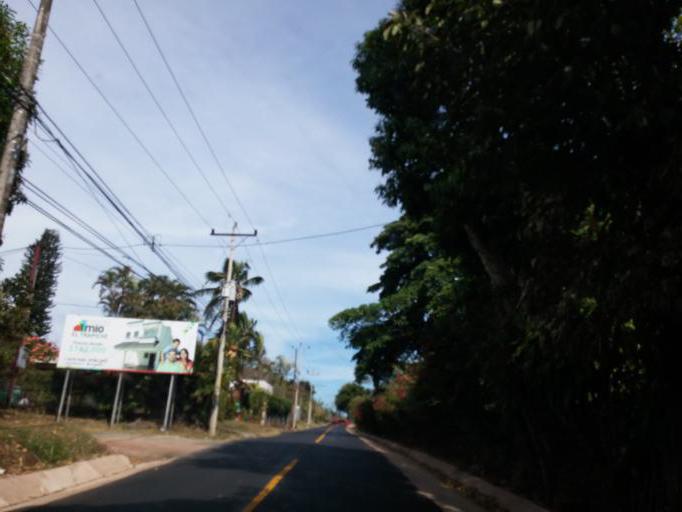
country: CR
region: Alajuela
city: Alajuela
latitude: 10.0277
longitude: -84.2236
